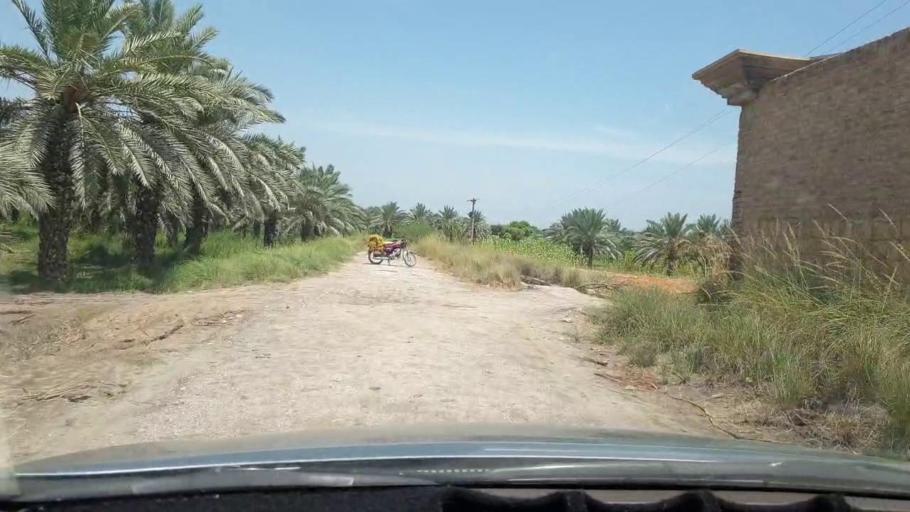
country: PK
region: Sindh
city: Khairpur
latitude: 27.4914
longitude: 68.7694
